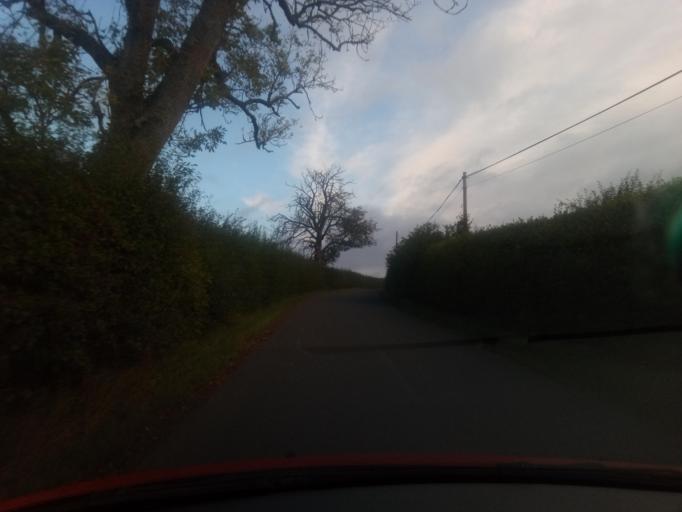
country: GB
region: Scotland
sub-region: The Scottish Borders
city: Jedburgh
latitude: 55.3791
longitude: -2.6468
